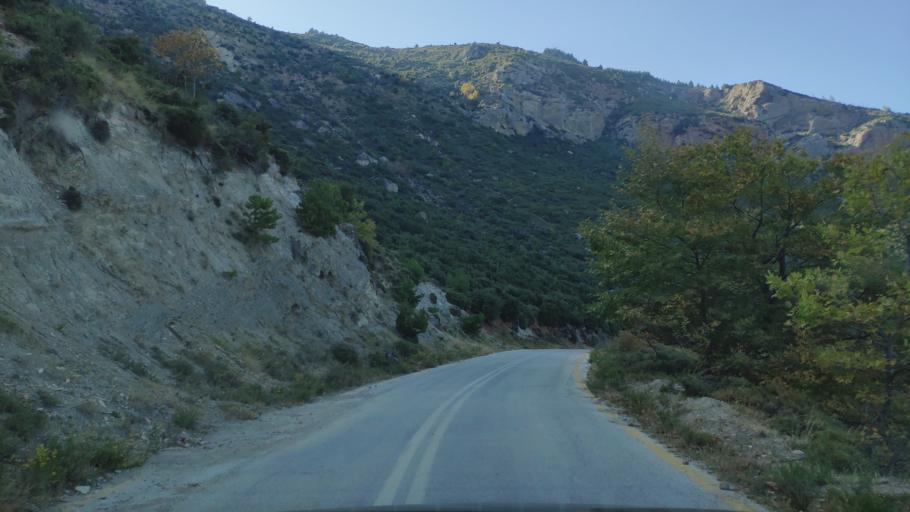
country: GR
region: West Greece
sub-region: Nomos Achaias
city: Aiyira
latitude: 38.0597
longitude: 22.3791
